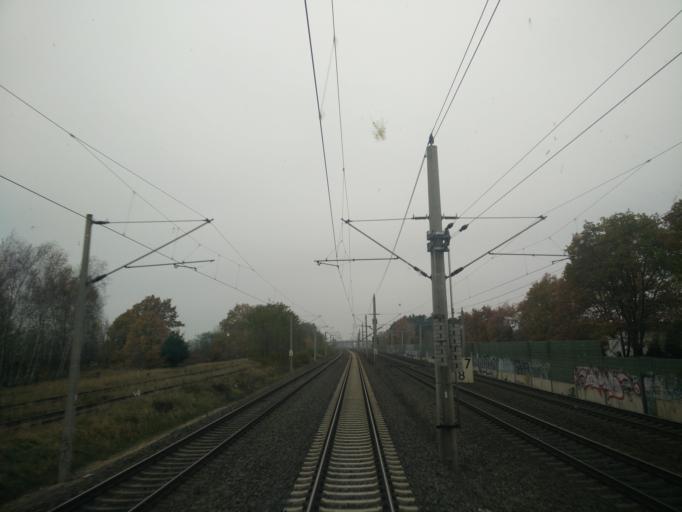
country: DE
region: Berlin
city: Staaken
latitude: 52.5389
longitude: 13.1245
